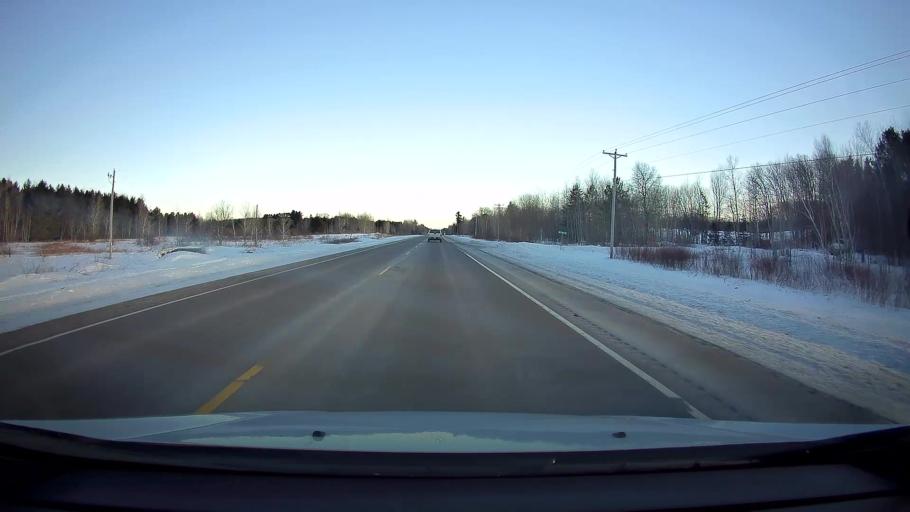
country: US
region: Wisconsin
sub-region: Washburn County
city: Shell Lake
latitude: 45.7142
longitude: -91.9417
